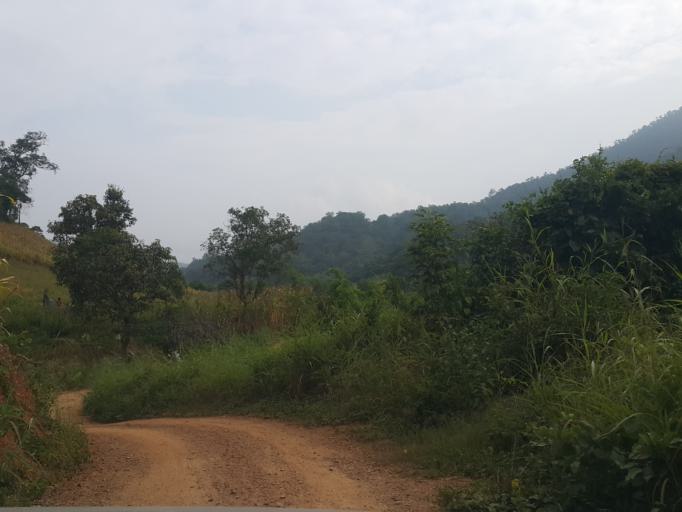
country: TH
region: Mae Hong Son
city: Wiang Nuea
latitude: 19.3899
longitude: 98.4677
